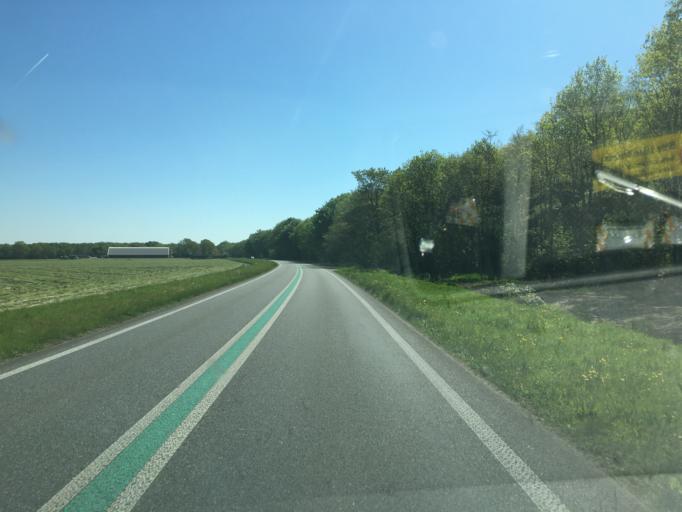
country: NL
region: Friesland
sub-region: Gemeente Gaasterlan-Sleat
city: Oudemirdum
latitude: 52.8739
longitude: 5.5203
